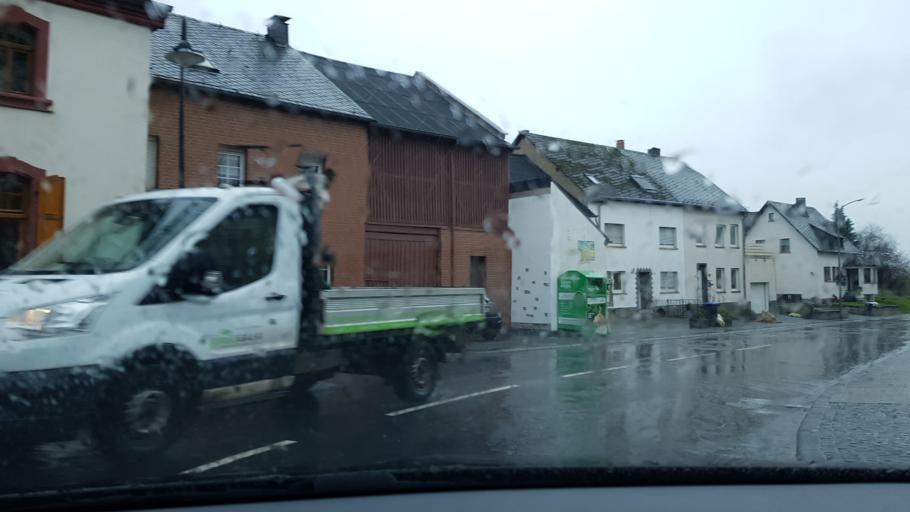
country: DE
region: Rheinland-Pfalz
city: Neuerburg
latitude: 49.9883
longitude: 6.9393
